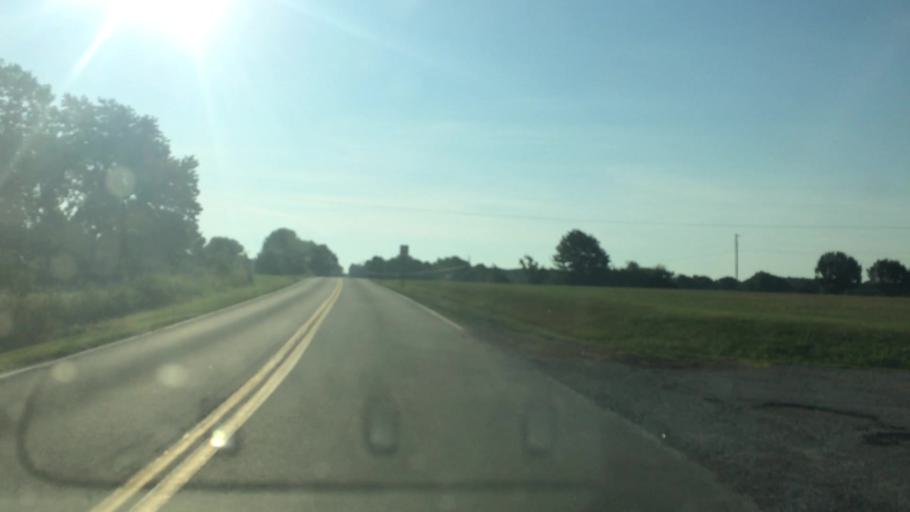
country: US
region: Missouri
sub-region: Greene County
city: Strafford
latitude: 37.2724
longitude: -93.2132
